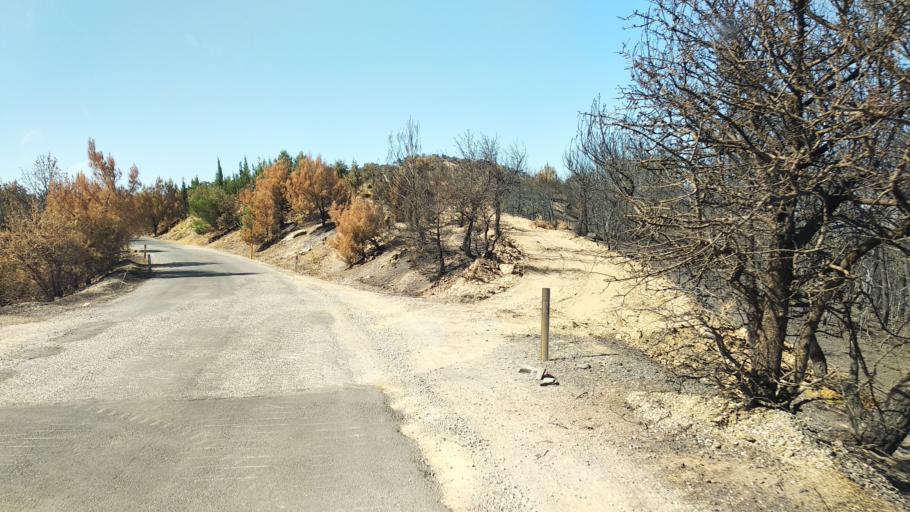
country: TR
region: Izmir
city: Gaziemir
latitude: 38.2903
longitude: 27.0019
